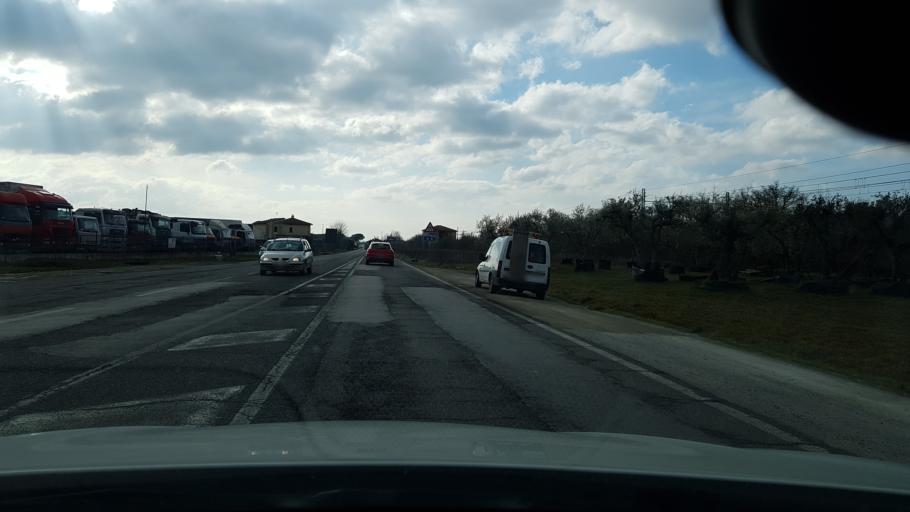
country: IT
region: Tuscany
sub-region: Province of Arezzo
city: Terontola
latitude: 43.1885
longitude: 12.0133
